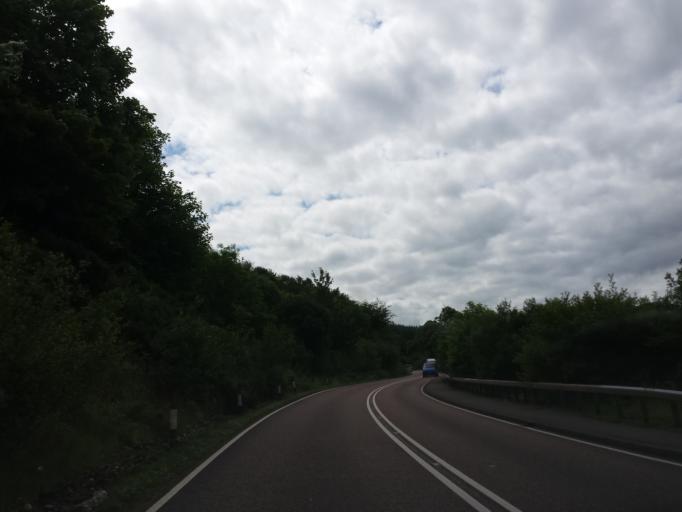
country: GB
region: Scotland
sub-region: Argyll and Bute
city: Oban
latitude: 56.4345
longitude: -5.4528
